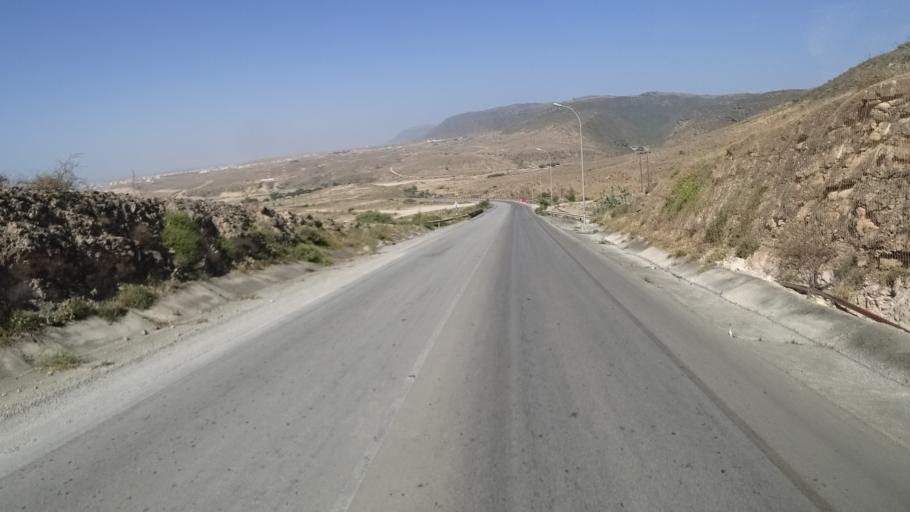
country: OM
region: Zufar
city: Salalah
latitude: 17.0653
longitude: 54.4434
